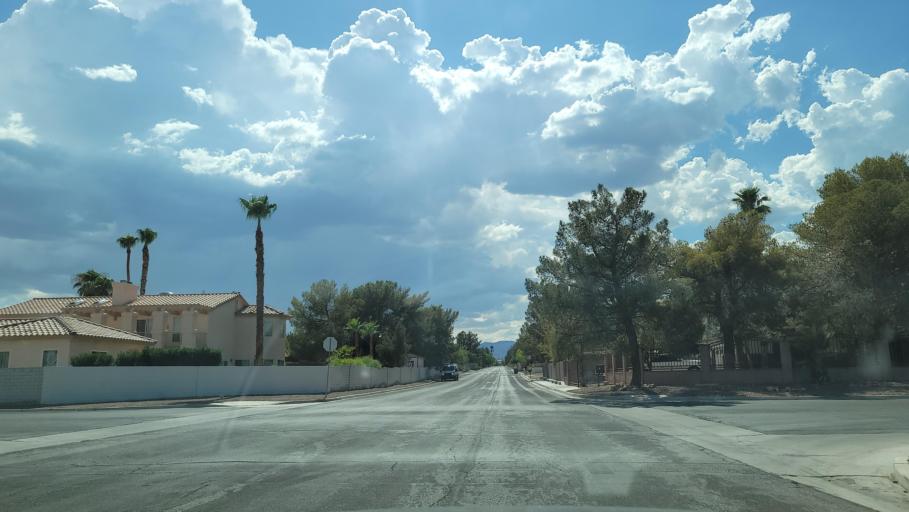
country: US
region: Nevada
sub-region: Clark County
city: Spring Valley
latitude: 36.1312
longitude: -115.2517
